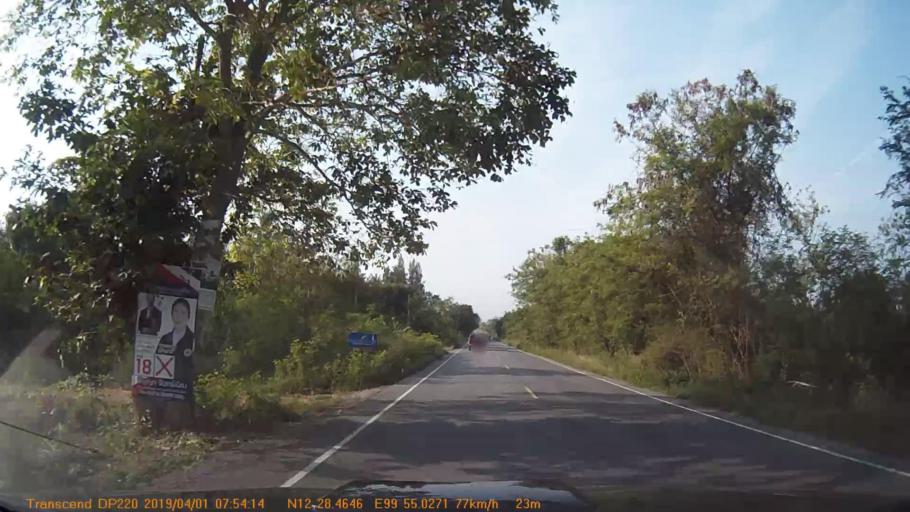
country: TH
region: Prachuap Khiri Khan
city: Pran Buri
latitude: 12.4740
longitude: 99.9171
